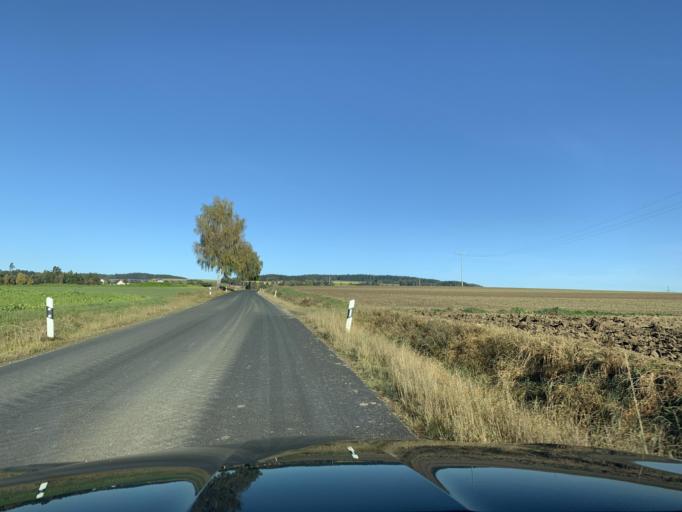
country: DE
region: Bavaria
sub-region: Upper Palatinate
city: Thanstein
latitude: 49.3964
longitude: 12.4711
